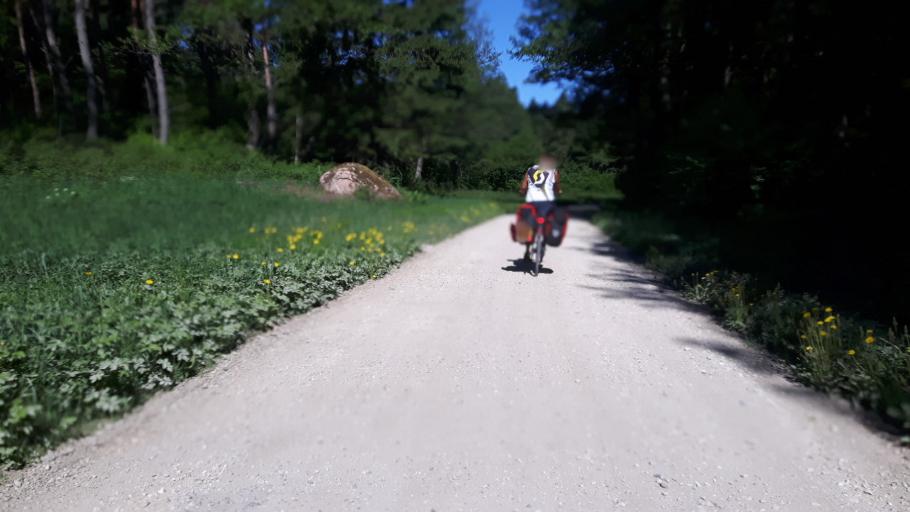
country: EE
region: Harju
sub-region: Loksa linn
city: Loksa
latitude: 59.5636
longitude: 25.8578
